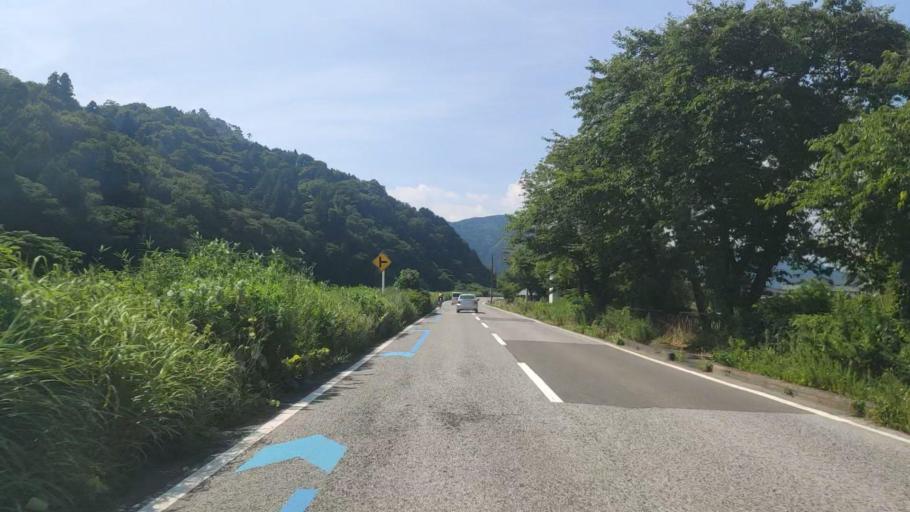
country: JP
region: Shiga Prefecture
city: Nagahama
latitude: 35.4751
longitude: 136.2115
